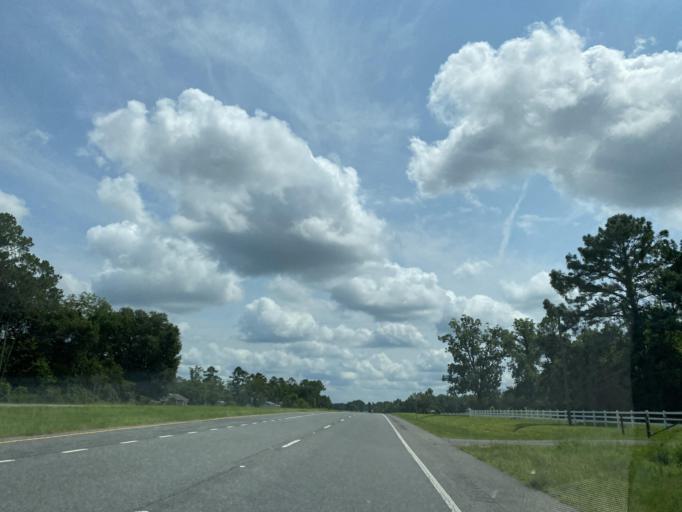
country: US
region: Georgia
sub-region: Ware County
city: Deenwood
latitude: 31.3171
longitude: -82.4569
